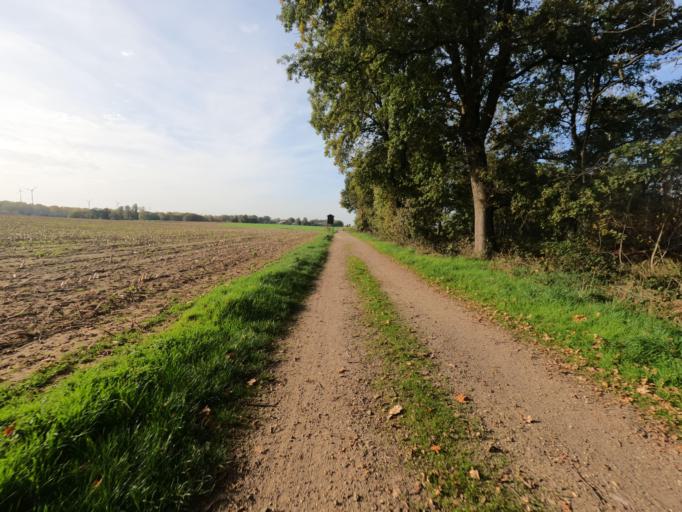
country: DE
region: North Rhine-Westphalia
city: Erkelenz
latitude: 51.0455
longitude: 6.2951
